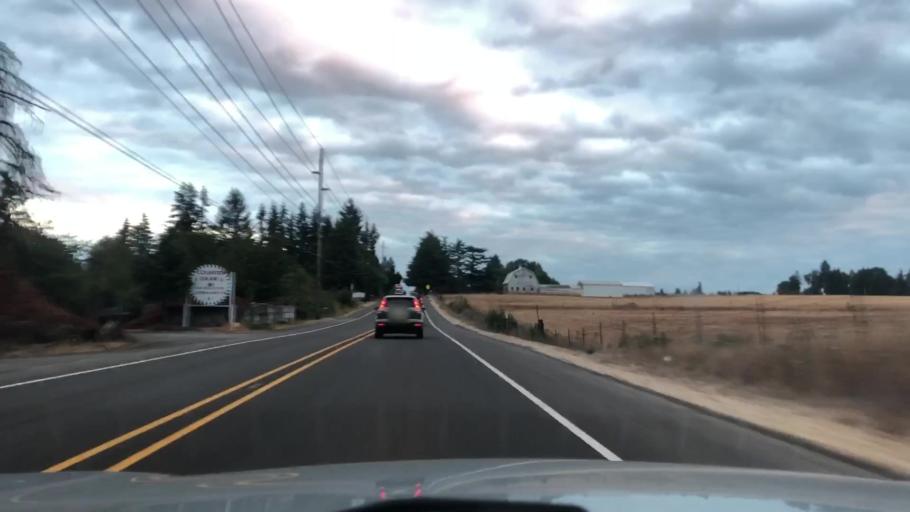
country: US
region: Oregon
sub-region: Clackamas County
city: Beavercreek
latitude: 45.2658
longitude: -122.5718
